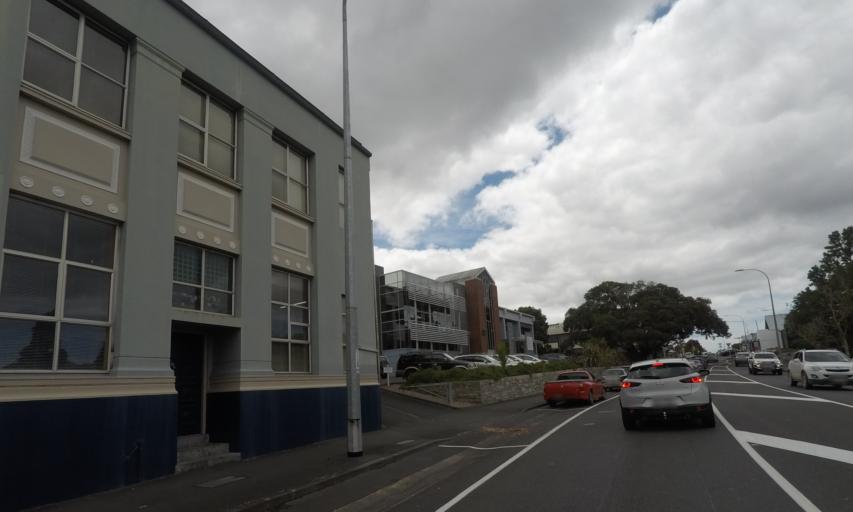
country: NZ
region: Northland
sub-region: Whangarei
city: Whangarei
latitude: -35.7230
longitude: 174.3199
